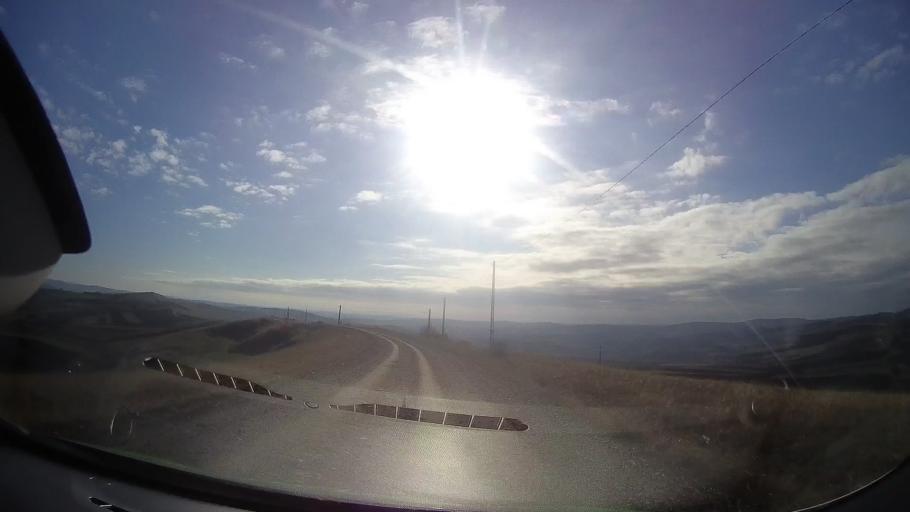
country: RO
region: Mures
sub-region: Comuna Saulia
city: Saulia
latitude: 46.5919
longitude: 24.2198
